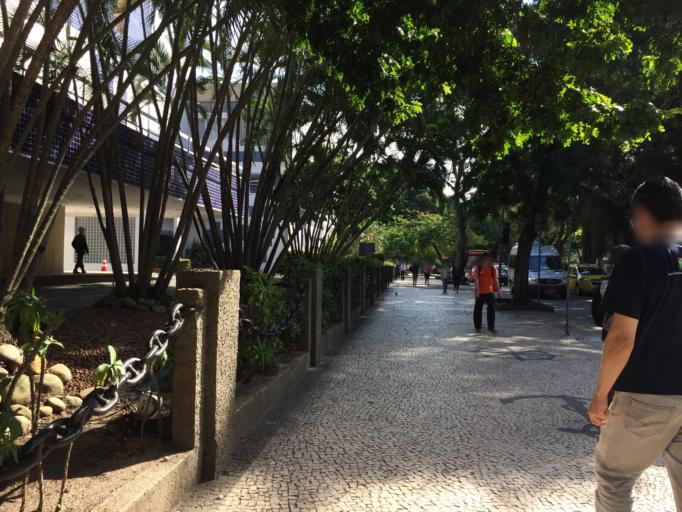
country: BR
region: Rio de Janeiro
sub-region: Rio De Janeiro
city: Rio de Janeiro
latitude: -22.9545
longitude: -43.1676
